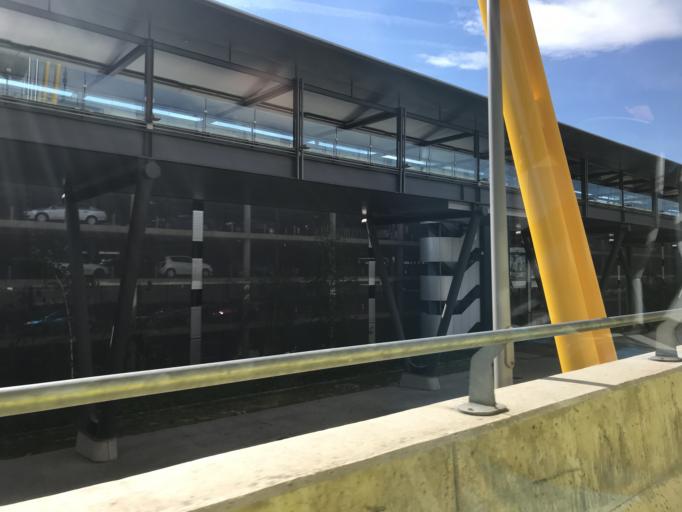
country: ES
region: Madrid
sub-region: Provincia de Madrid
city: Barajas de Madrid
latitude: 40.4922
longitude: -3.5940
